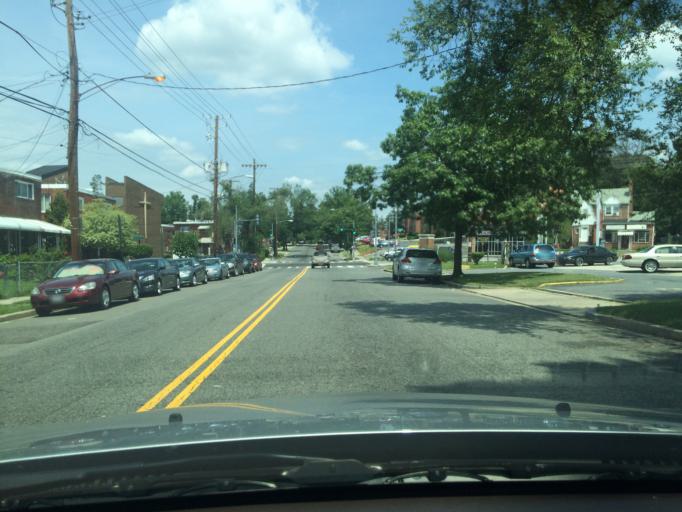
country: US
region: Maryland
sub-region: Prince George's County
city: Chillum
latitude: 38.9610
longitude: -76.9965
